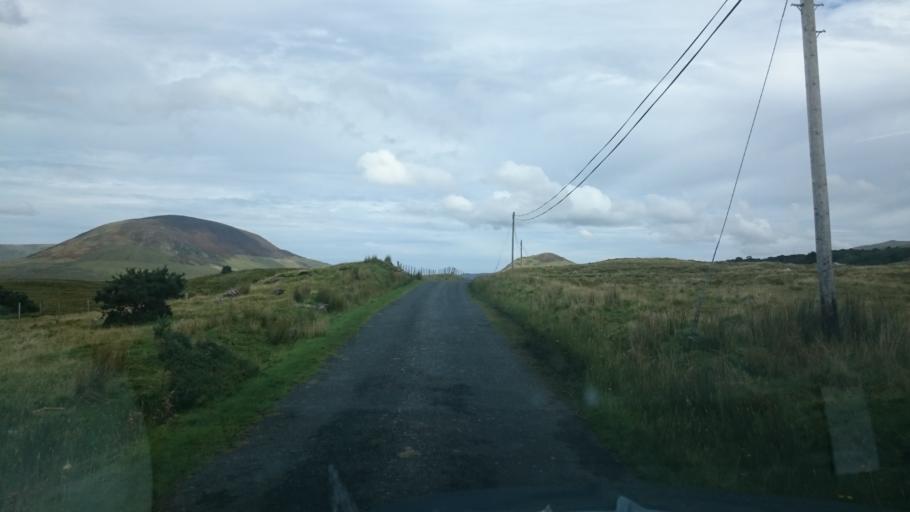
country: IE
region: Connaught
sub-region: Maigh Eo
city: Westport
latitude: 53.9409
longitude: -9.5680
